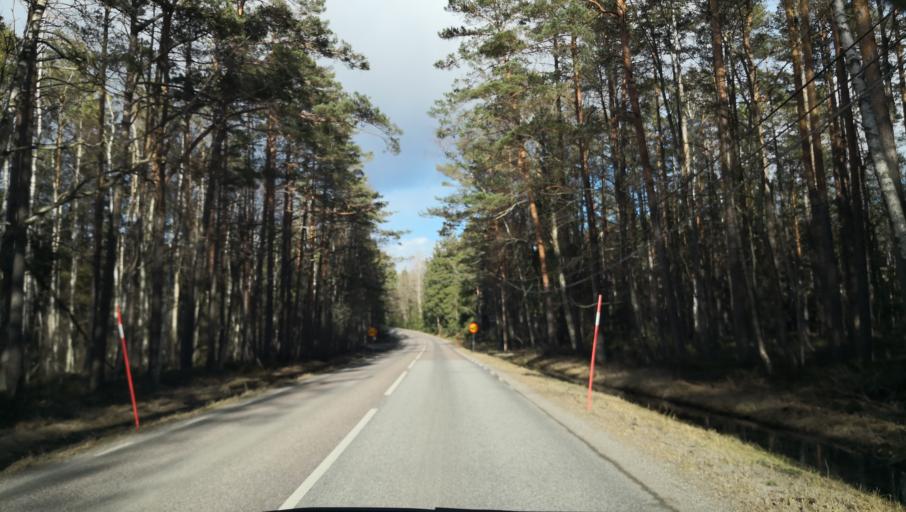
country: SE
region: Stockholm
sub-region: Varmdo Kommun
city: Hemmesta
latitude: 59.2794
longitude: 18.4781
